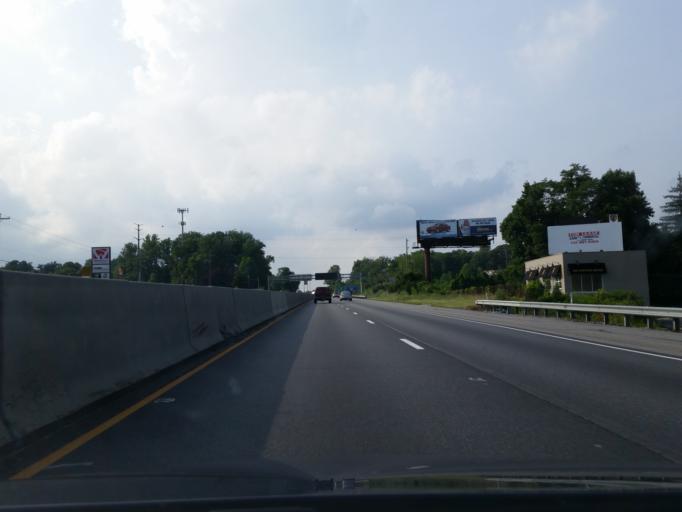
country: US
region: Pennsylvania
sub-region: York County
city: Valley Green
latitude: 40.1228
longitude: -76.7901
